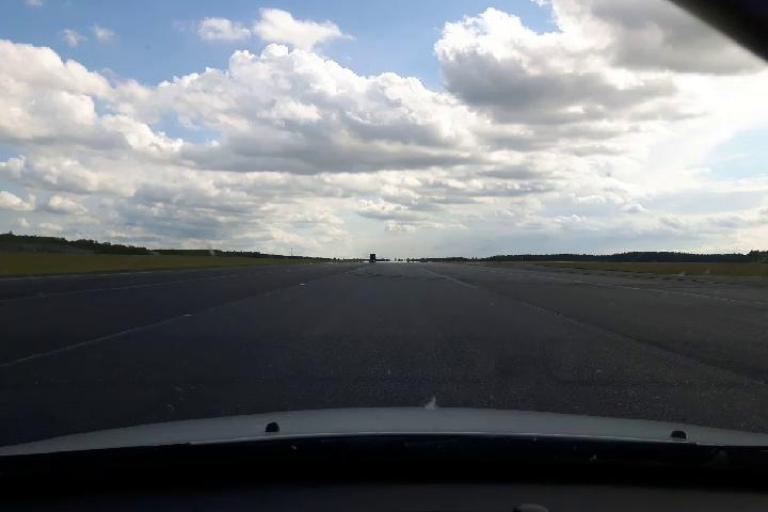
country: SE
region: Stockholm
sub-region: Sigtuna Kommun
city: Rosersberg
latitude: 59.6351
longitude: 17.9538
